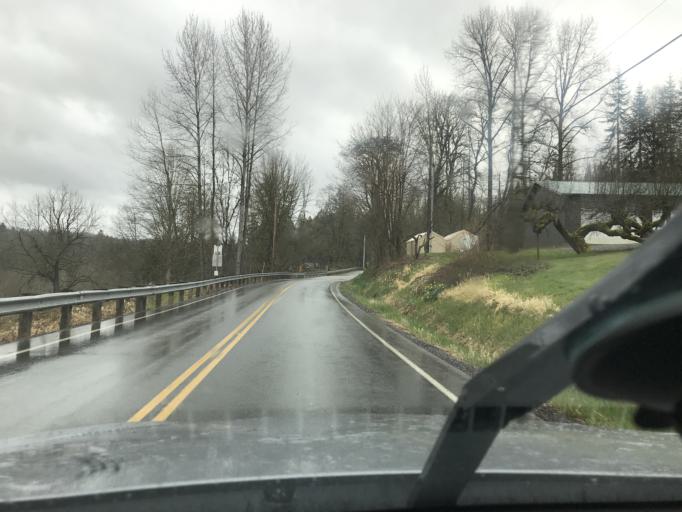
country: US
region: Washington
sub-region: King County
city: Ames Lake
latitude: 47.6658
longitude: -121.9717
